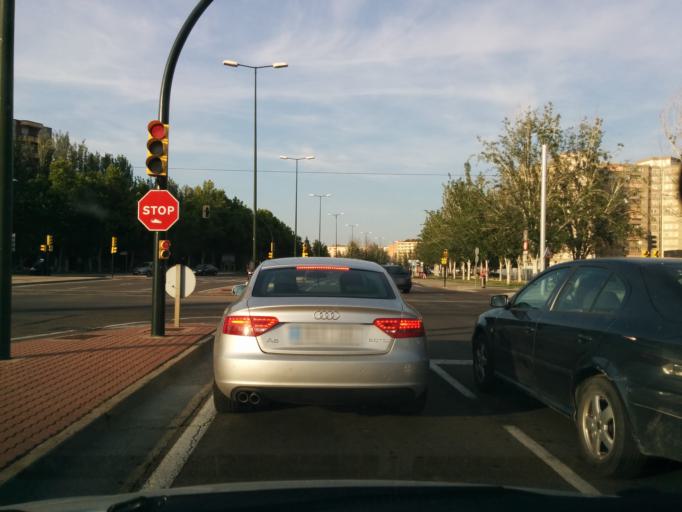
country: ES
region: Aragon
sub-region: Provincia de Zaragoza
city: Zaragoza
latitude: 41.6656
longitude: -0.8853
